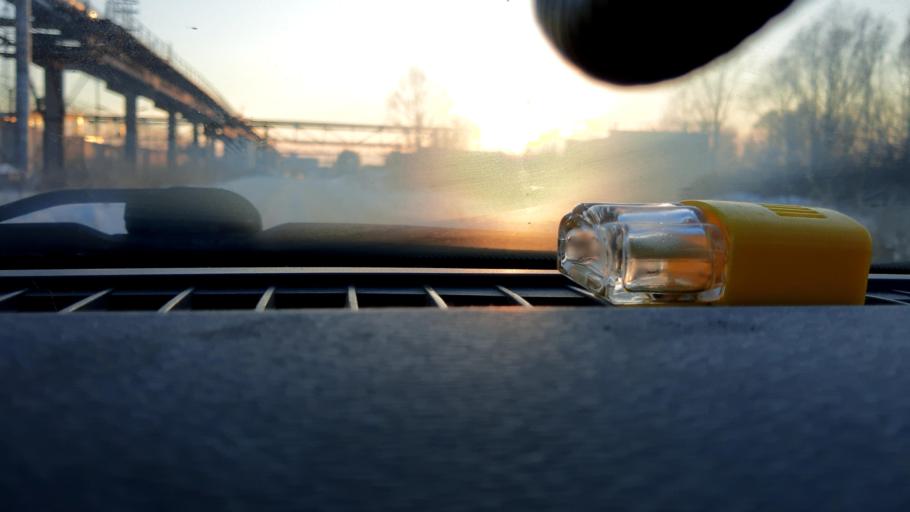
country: RU
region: Bashkortostan
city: Iglino
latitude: 54.7647
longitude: 56.2454
